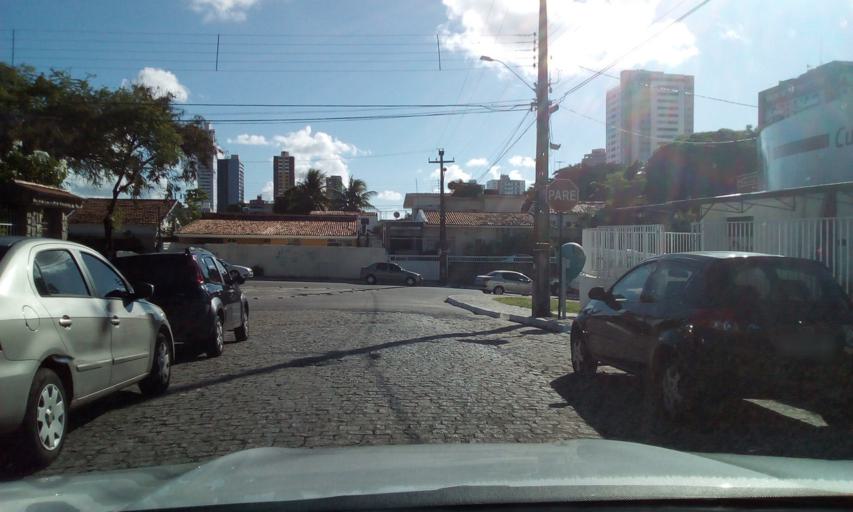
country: BR
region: Paraiba
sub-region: Joao Pessoa
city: Joao Pessoa
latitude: -7.1201
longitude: -34.8353
